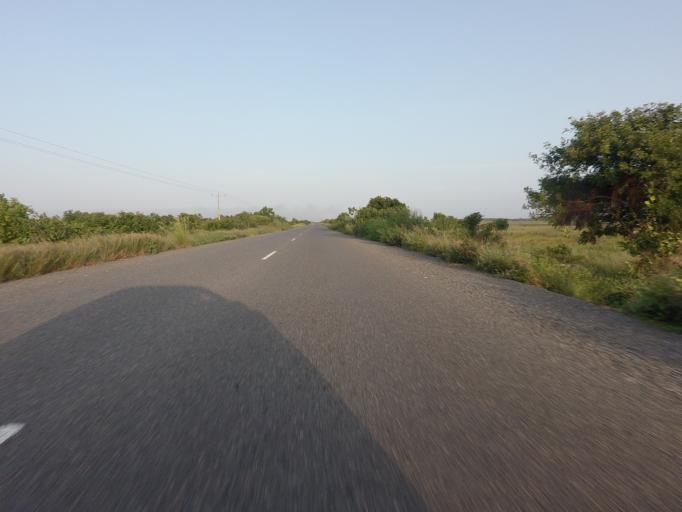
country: GH
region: Volta
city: Anloga
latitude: 5.8543
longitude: 0.7693
